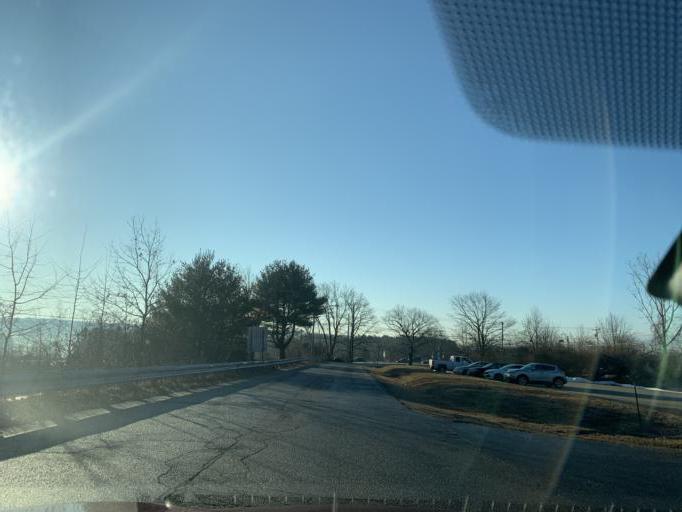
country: US
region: New Hampshire
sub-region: Rockingham County
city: Derry
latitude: 42.8700
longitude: -71.3440
